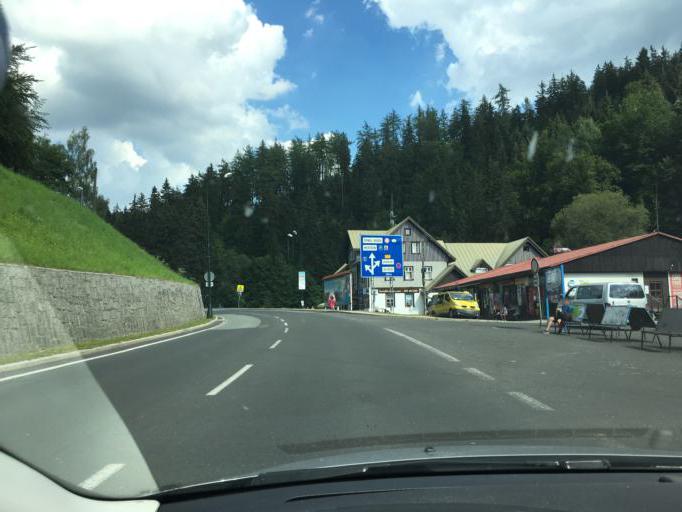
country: CZ
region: Kralovehradecky
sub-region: Okres Trutnov
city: Spindleruv Mlyn
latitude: 50.7244
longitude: 15.6035
